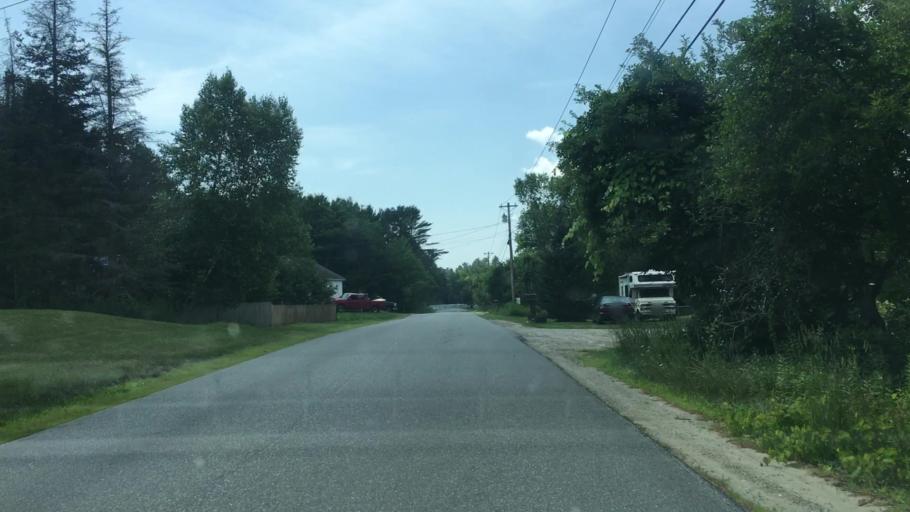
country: US
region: New Hampshire
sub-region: Grafton County
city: Enfield
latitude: 43.6730
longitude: -72.0976
